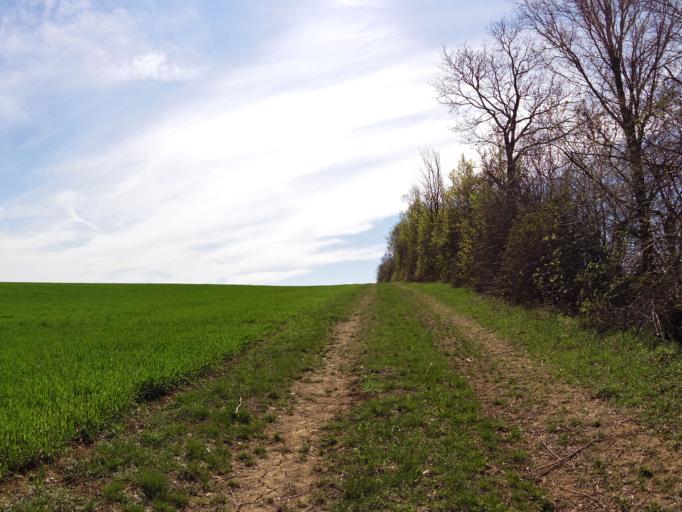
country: DE
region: Bavaria
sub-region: Regierungsbezirk Unterfranken
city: Rottendorf
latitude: 49.7893
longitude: 10.0596
